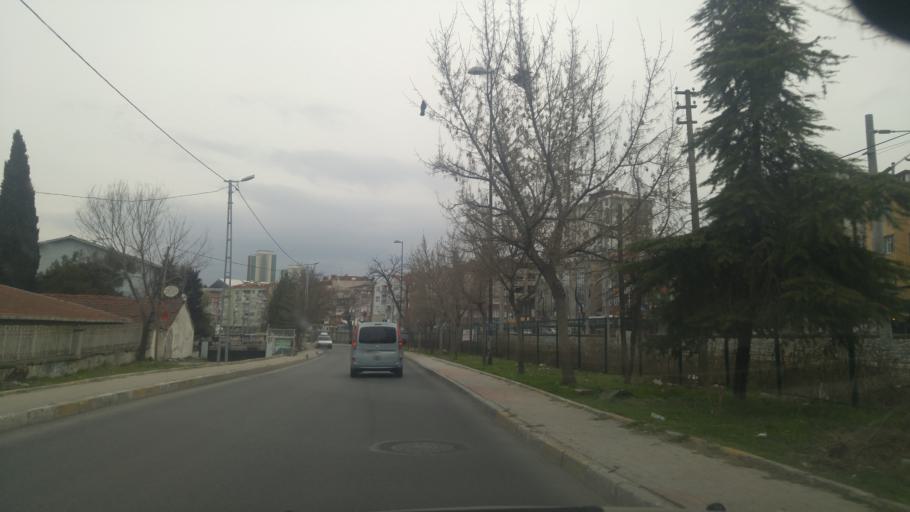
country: TR
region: Istanbul
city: Mahmutbey
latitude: 41.0084
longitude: 28.7744
